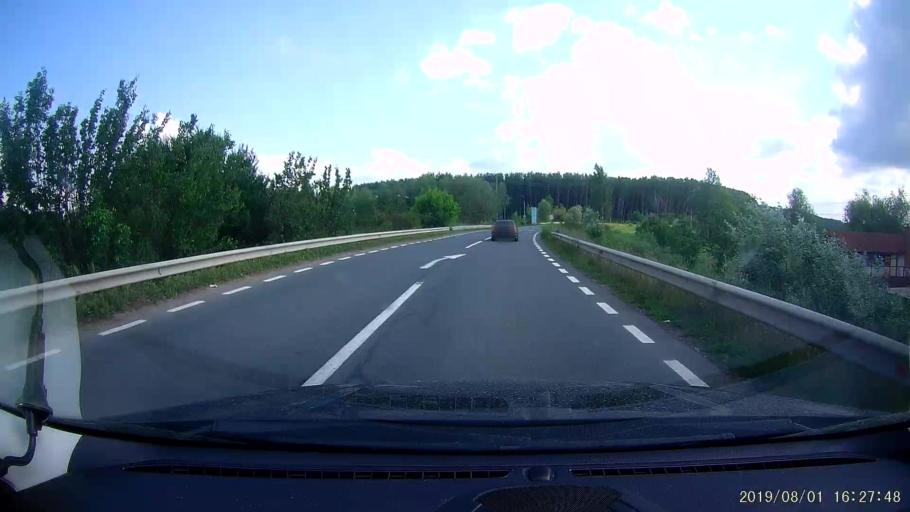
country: RO
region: Calarasi
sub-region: Municipiul Calarasi
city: Calarasi
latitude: 44.1584
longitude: 27.3171
